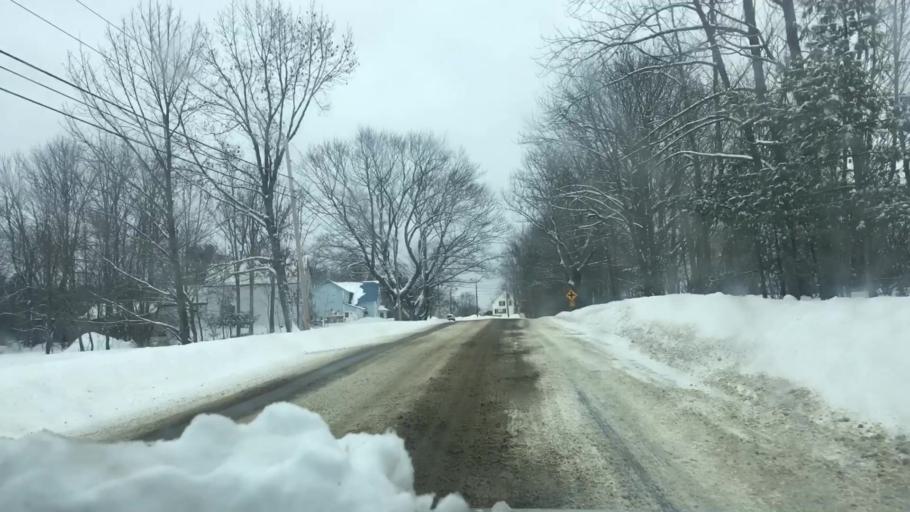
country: US
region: Maine
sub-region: Penobscot County
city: Bradford
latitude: 45.0103
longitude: -69.0007
